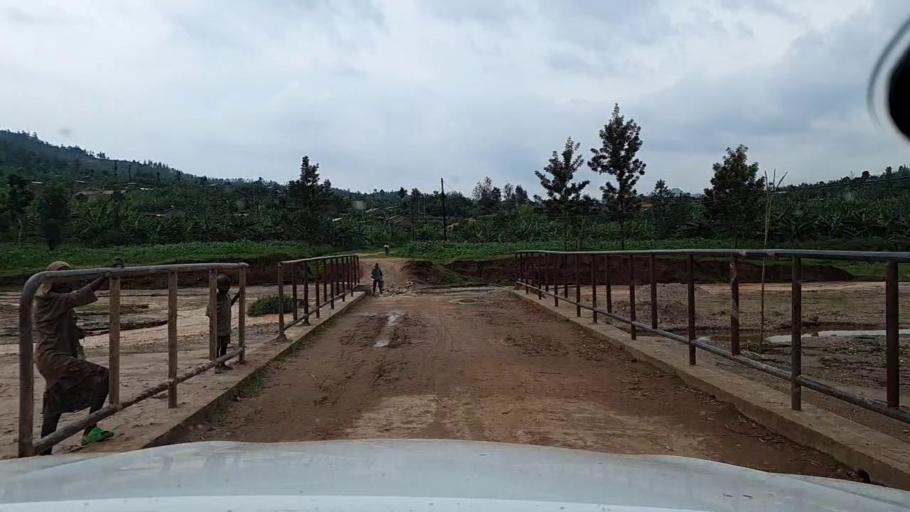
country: RW
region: Kigali
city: Kigali
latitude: -1.8783
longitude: 29.9269
